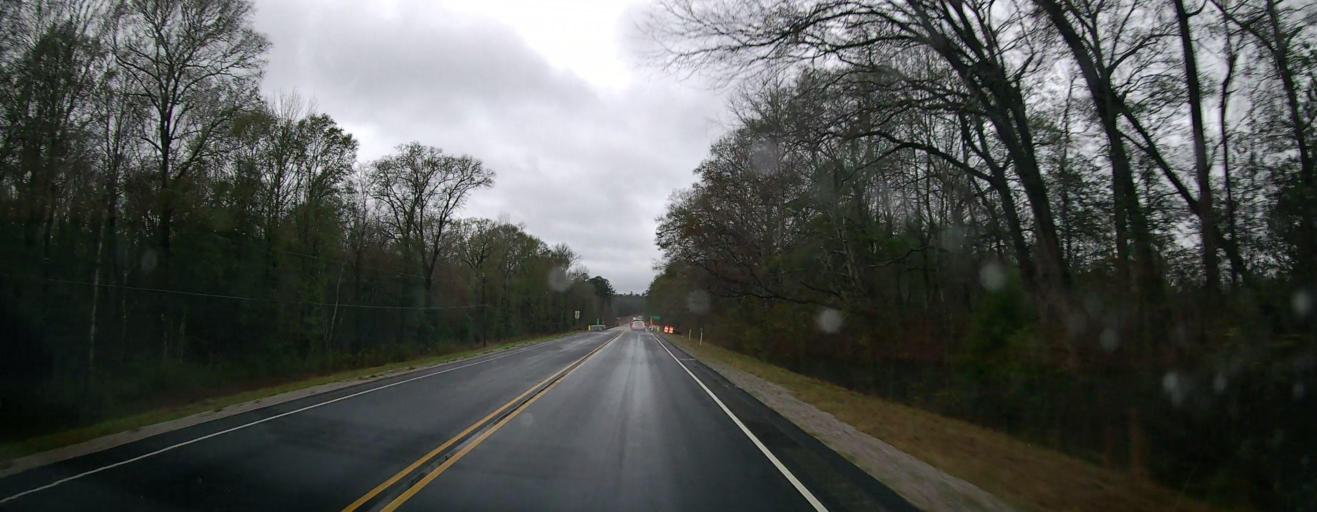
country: US
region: Alabama
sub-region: Chilton County
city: Clanton
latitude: 32.6137
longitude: -86.7240
